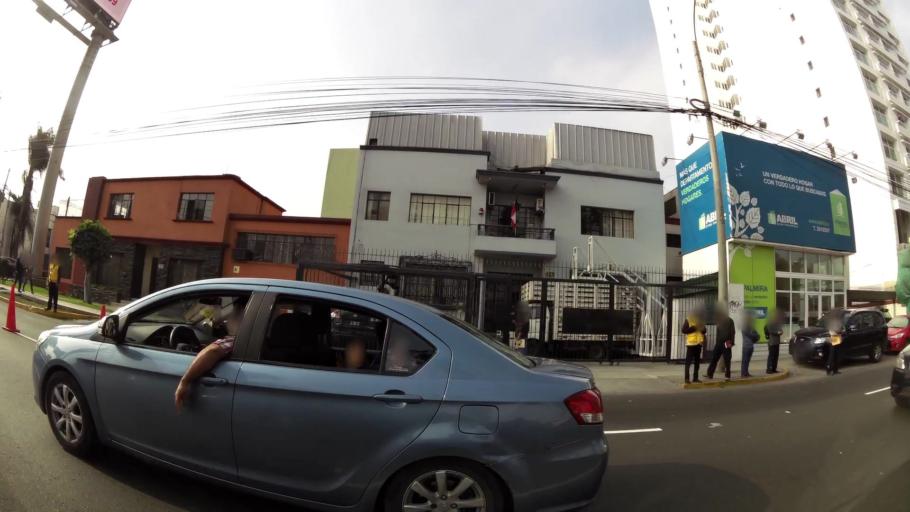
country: PE
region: Lima
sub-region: Lima
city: San Isidro
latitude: -12.0888
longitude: -77.0594
